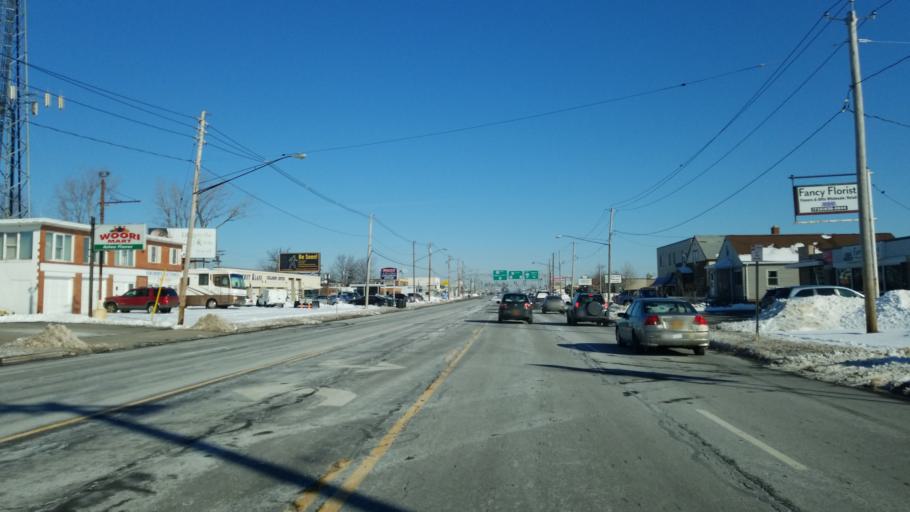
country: US
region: New York
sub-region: Erie County
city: Amherst
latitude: 42.9770
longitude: -78.8231
